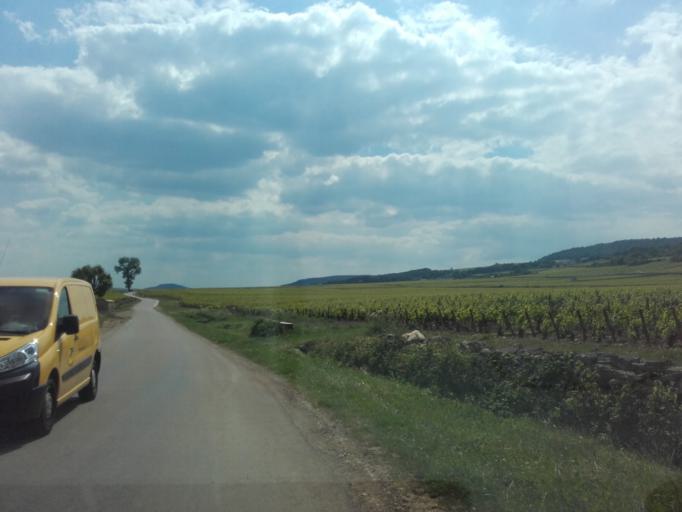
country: FR
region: Bourgogne
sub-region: Departement de la Cote-d'Or
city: Meursault
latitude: 46.9649
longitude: 4.7629
